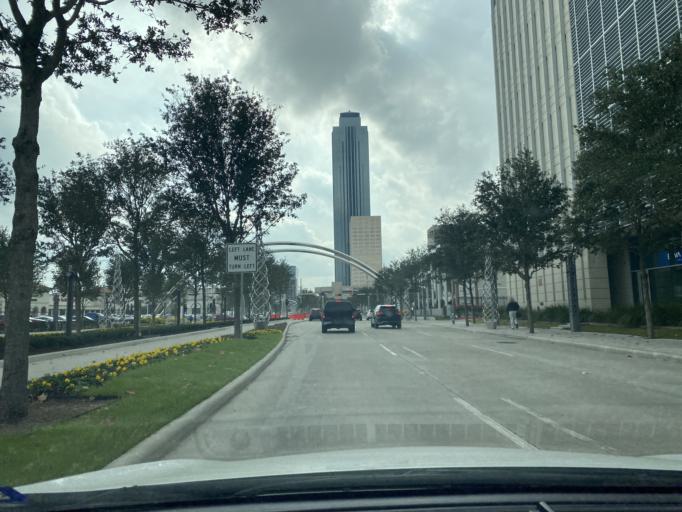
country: US
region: Texas
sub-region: Harris County
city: West University Place
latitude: 29.7435
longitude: -95.4612
